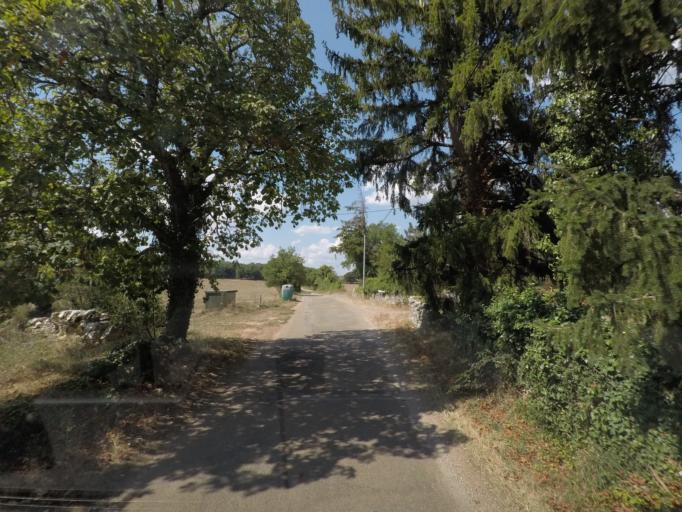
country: FR
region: Midi-Pyrenees
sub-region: Departement du Lot
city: Lalbenque
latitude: 44.5239
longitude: 1.6231
